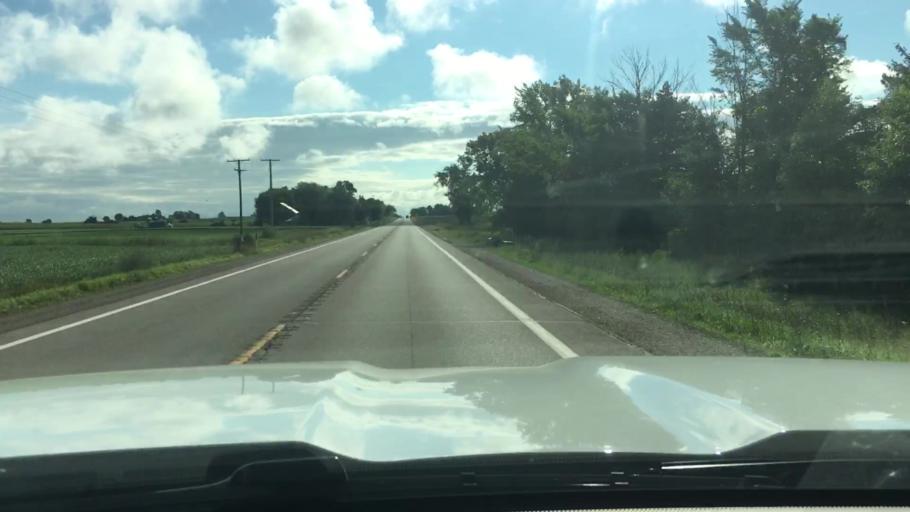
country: US
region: Michigan
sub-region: Tuscola County
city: Cass City
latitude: 43.5997
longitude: -83.2302
